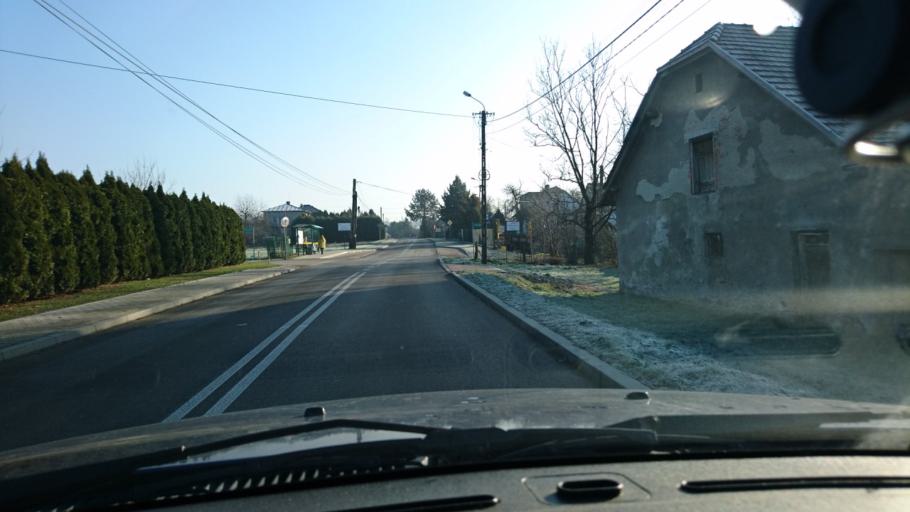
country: PL
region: Silesian Voivodeship
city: Janowice
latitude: 49.8926
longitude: 19.0784
